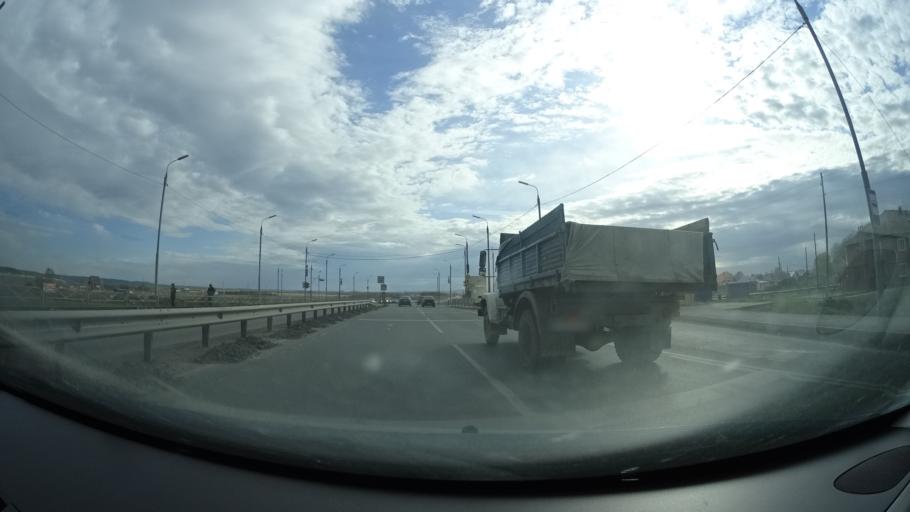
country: RU
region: Perm
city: Kultayevo
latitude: 57.9086
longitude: 55.9907
